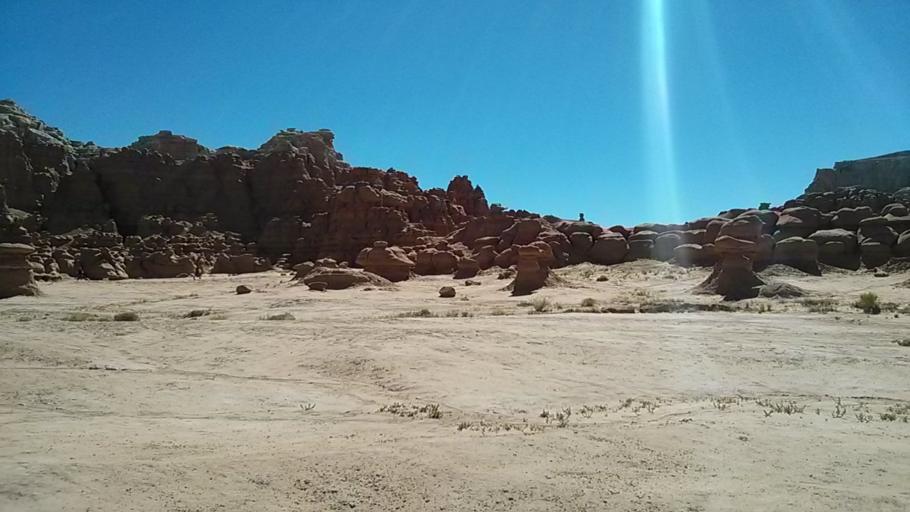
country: US
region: Utah
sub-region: Emery County
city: Ferron
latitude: 38.5641
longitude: -110.6990
